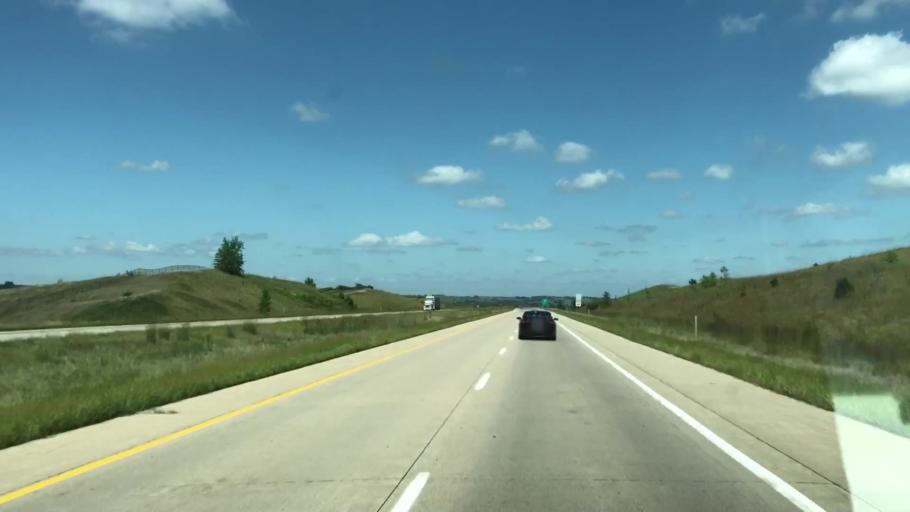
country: US
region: Iowa
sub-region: Woodbury County
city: Sioux City
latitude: 42.5272
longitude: -96.3388
